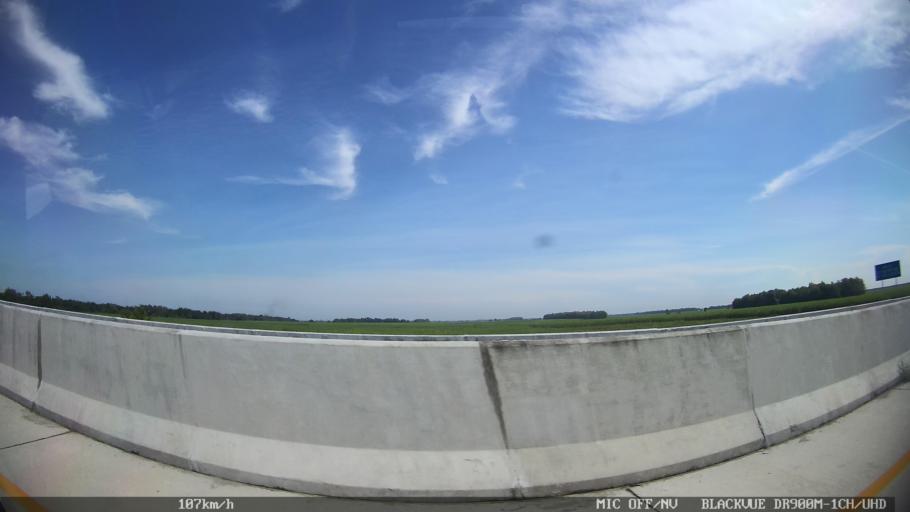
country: ID
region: North Sumatra
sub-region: Kabupaten Langkat
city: Stabat
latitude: 3.7134
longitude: 98.5147
